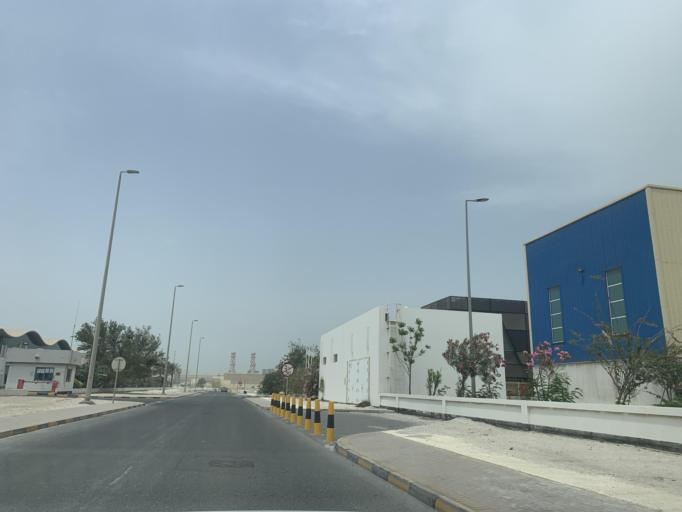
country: BH
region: Muharraq
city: Al Hadd
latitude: 26.2181
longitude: 50.6696
